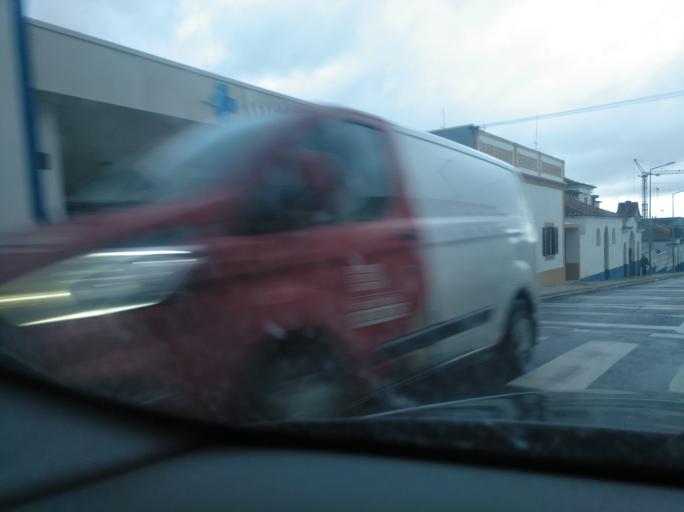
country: PT
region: Beja
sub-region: Aljustrel
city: Aljustrel
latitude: 37.8795
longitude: -8.1605
